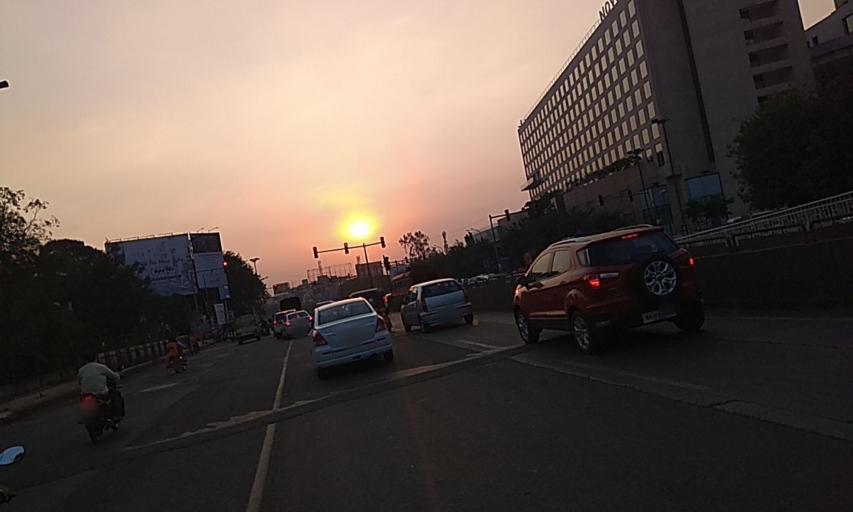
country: IN
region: Maharashtra
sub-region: Pune Division
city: Lohogaon
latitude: 18.5588
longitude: 73.9124
